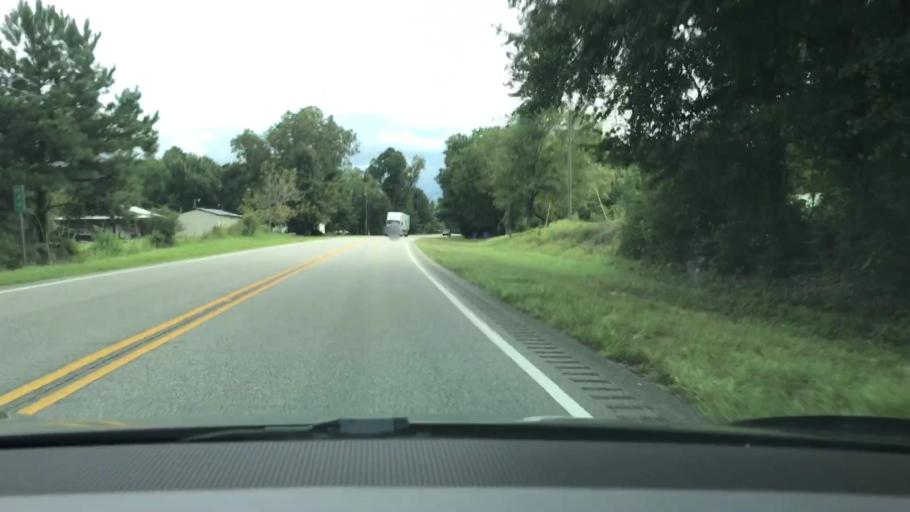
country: US
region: Alabama
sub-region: Coffee County
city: Elba
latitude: 31.5552
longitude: -86.0144
